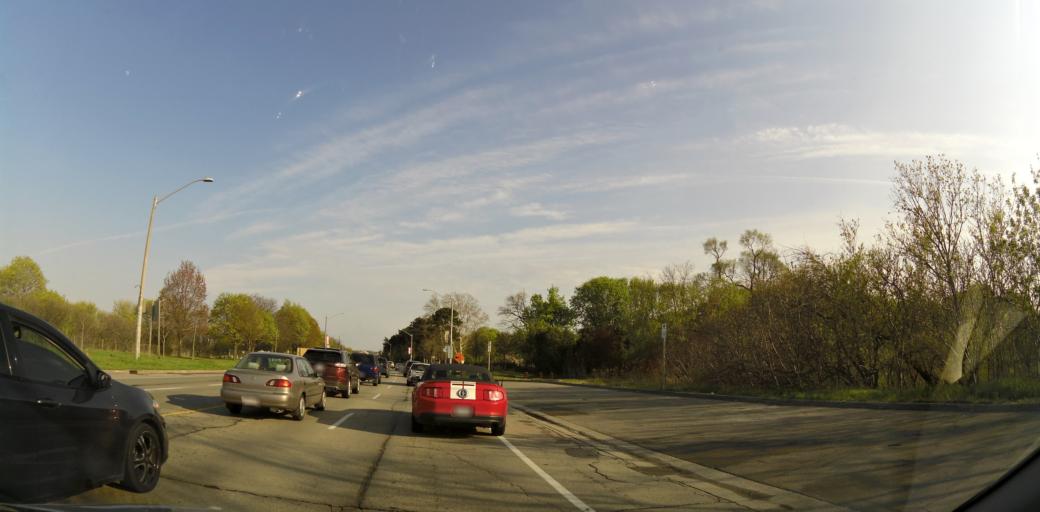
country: CA
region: Ontario
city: Hamilton
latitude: 43.2778
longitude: -79.8904
